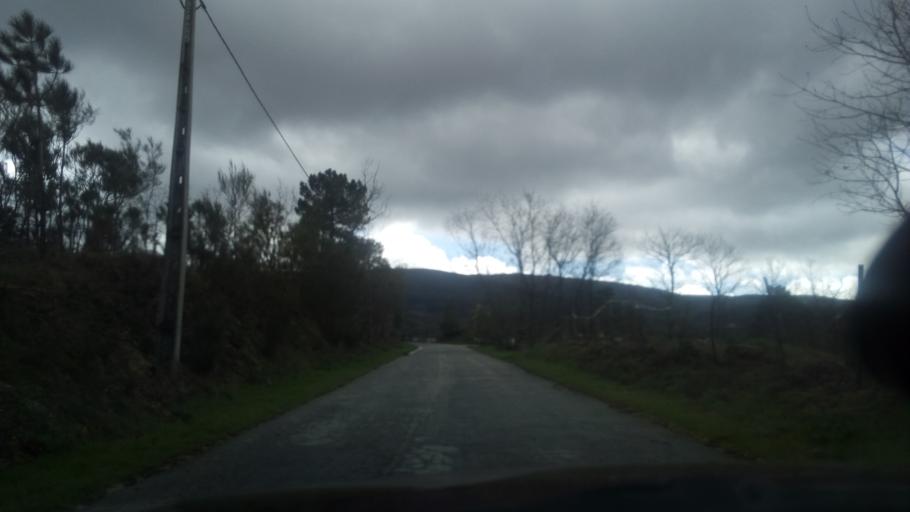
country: PT
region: Guarda
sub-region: Celorico da Beira
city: Celorico da Beira
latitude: 40.5624
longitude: -7.4585
